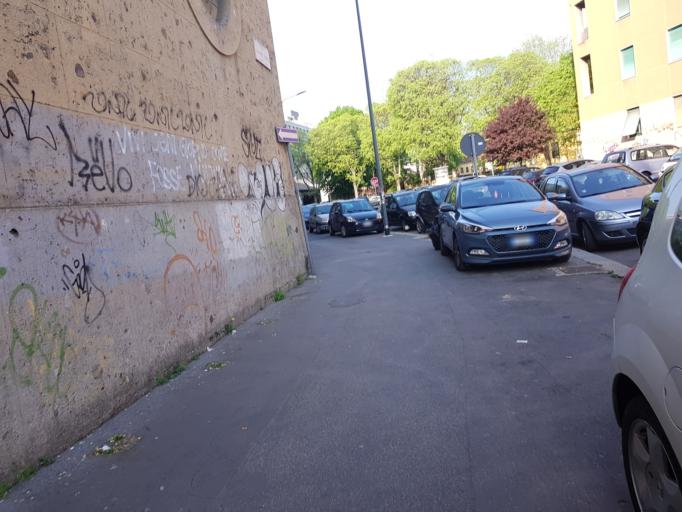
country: IT
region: Lombardy
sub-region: Citta metropolitana di Milano
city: Milano
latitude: 45.4806
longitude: 9.2310
